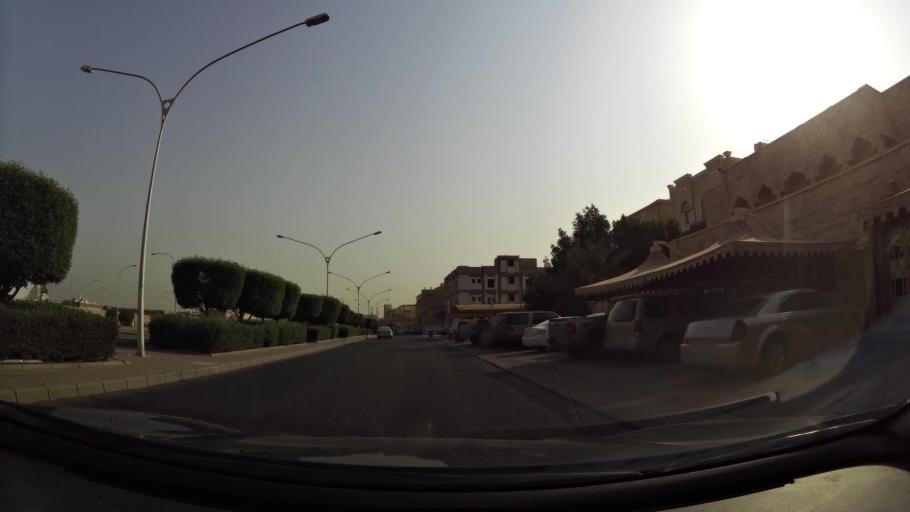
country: KW
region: Al Ahmadi
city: Al Manqaf
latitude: 29.1024
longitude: 48.1049
